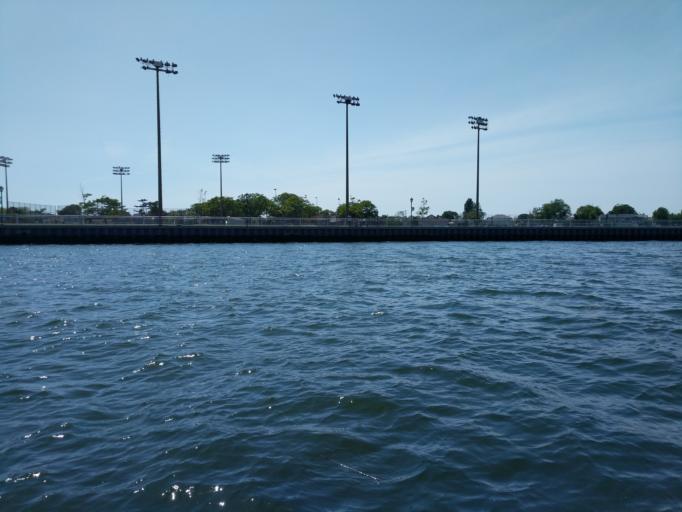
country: US
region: New York
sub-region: Nassau County
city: Barnum Island
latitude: 40.5999
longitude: -73.6447
